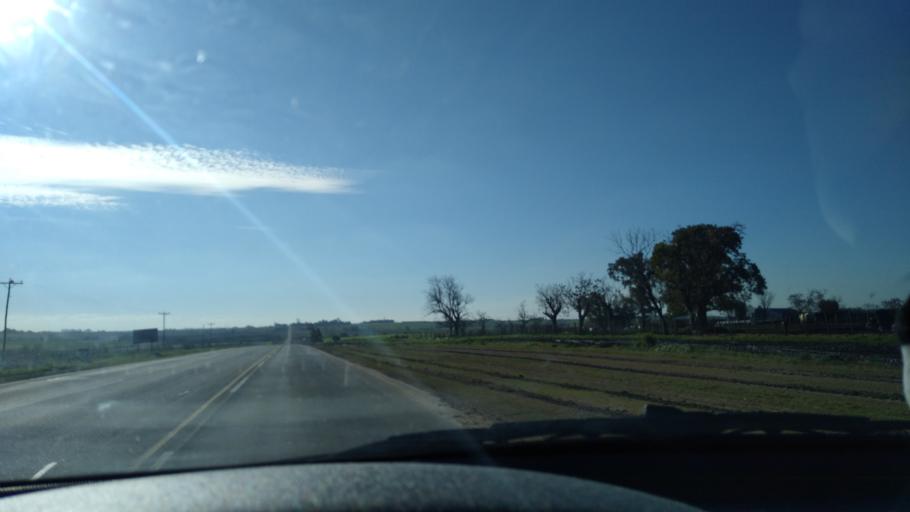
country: AR
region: Entre Rios
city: Aranguren
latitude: -32.3880
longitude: -60.3331
